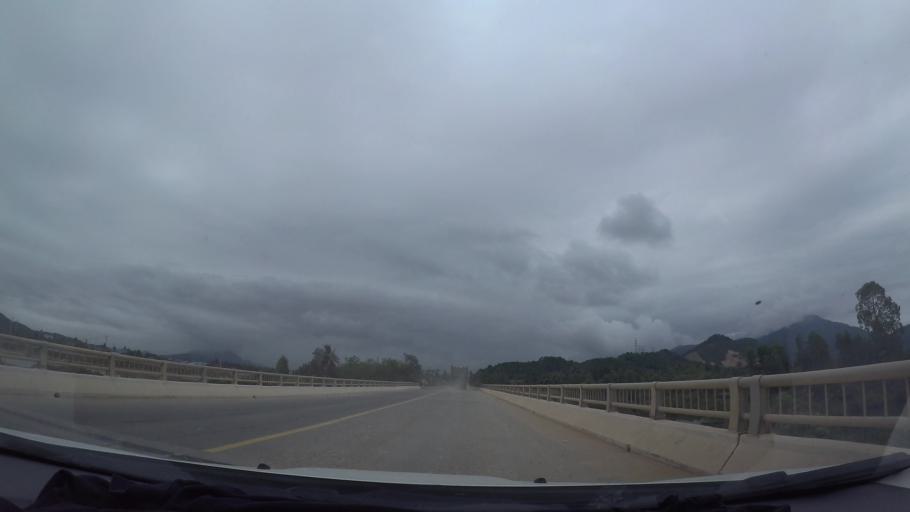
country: VN
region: Da Nang
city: Lien Chieu
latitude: 16.1065
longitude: 108.1023
